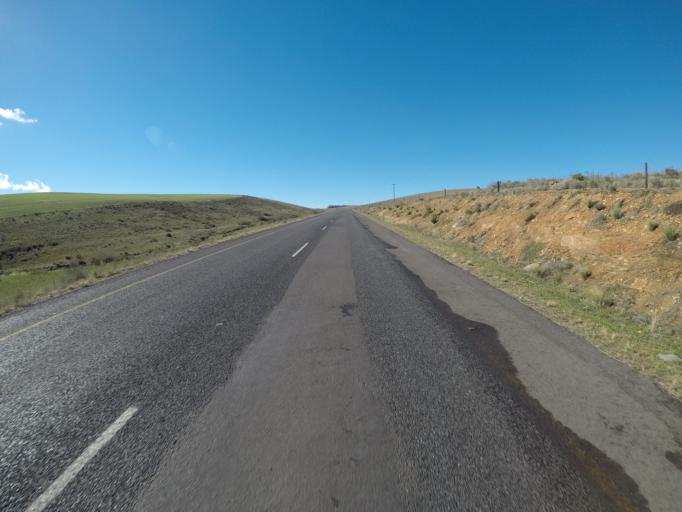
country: ZA
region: Western Cape
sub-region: Overberg District Municipality
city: Caledon
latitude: -34.1479
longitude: 19.4870
